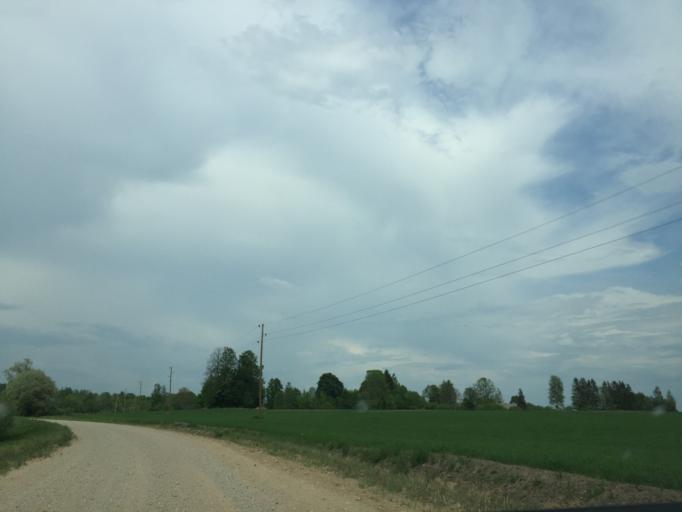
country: LV
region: Livani
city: Livani
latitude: 56.5799
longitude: 26.1807
